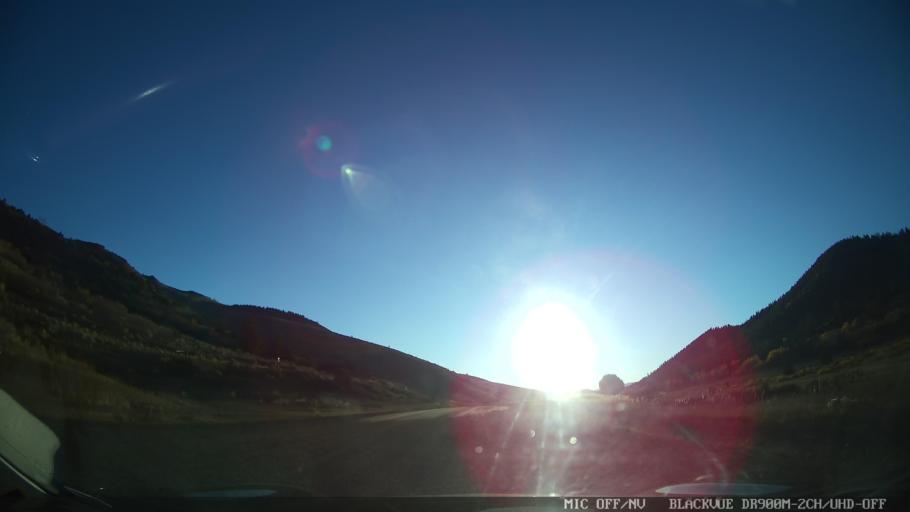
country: US
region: Colorado
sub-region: Grand County
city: Kremmling
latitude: 39.9933
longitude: -106.4634
